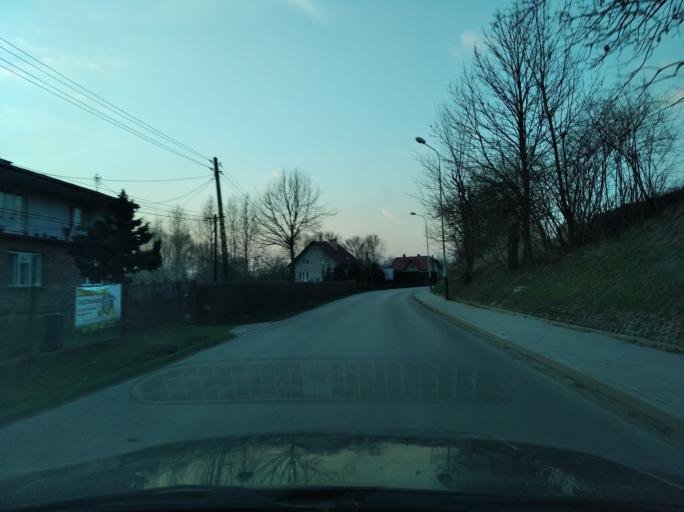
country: PL
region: Subcarpathian Voivodeship
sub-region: Powiat przeworski
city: Przeworsk
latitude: 50.0455
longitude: 22.5030
